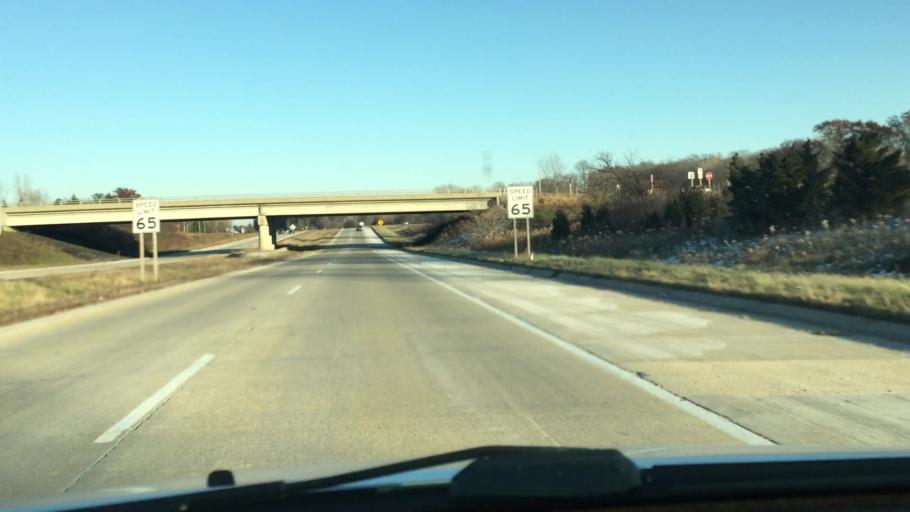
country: US
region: Wisconsin
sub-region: Waukesha County
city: Okauchee Lake
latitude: 43.1079
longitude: -88.4628
